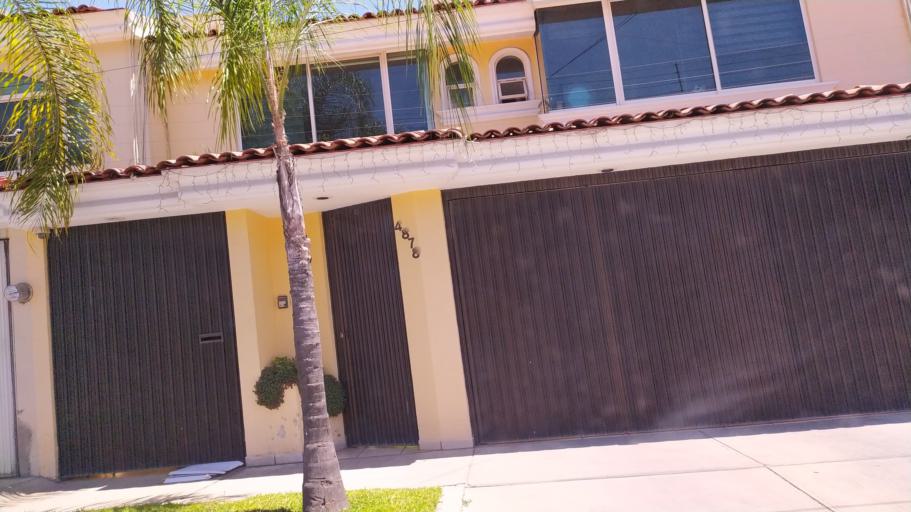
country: MX
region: Jalisco
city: Guadalajara
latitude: 20.6855
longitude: -103.4180
